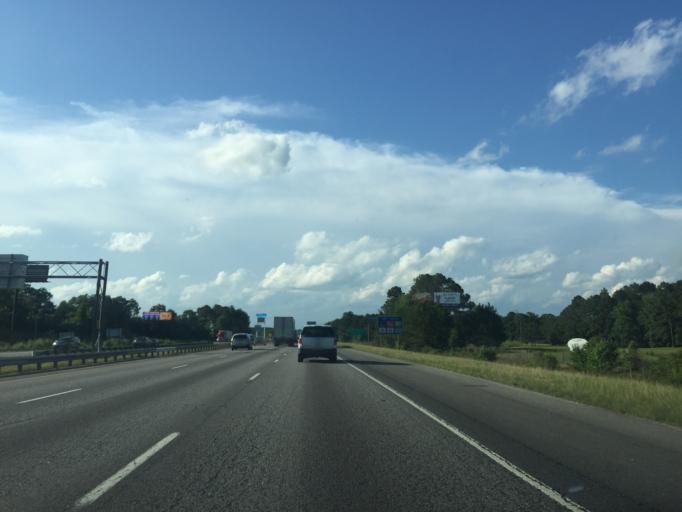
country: US
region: Georgia
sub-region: Chatham County
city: Pooler
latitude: 32.1264
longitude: -81.2392
